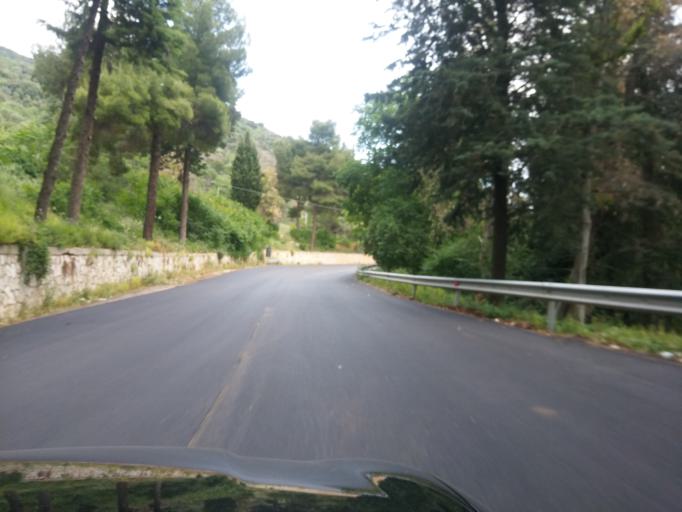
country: IT
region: Apulia
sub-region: Provincia di Foggia
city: Rignano Garganico
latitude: 41.7189
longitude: 15.5797
